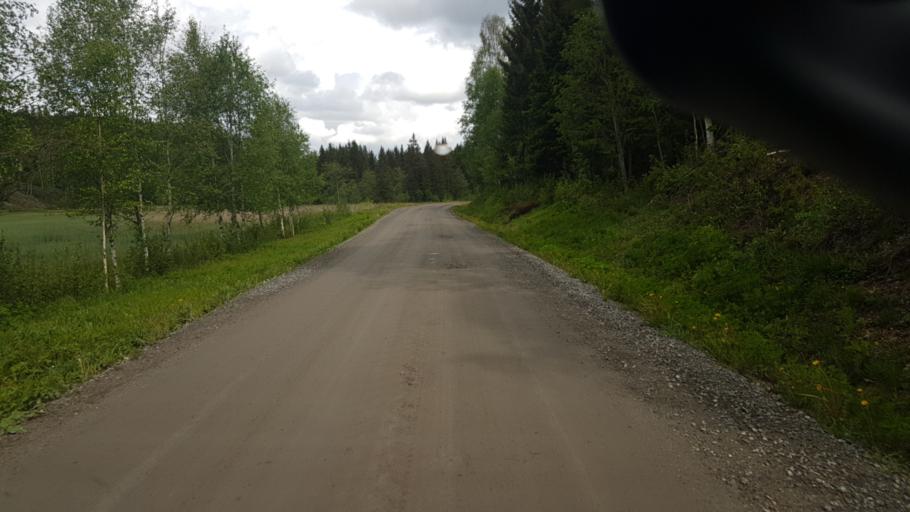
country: NO
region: Ostfold
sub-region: Romskog
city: Romskog
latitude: 59.6736
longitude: 11.9334
